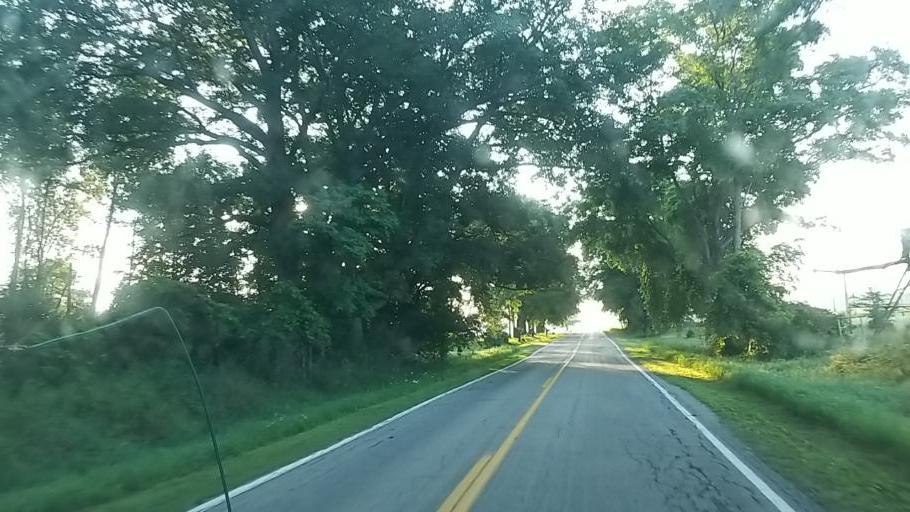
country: US
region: Michigan
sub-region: Montcalm County
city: Howard City
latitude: 43.3593
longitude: -85.3920
